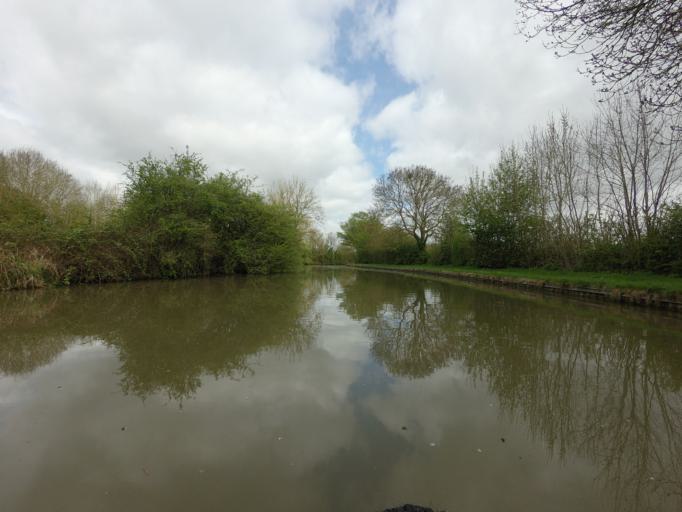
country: GB
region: England
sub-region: Milton Keynes
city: Water Eaton
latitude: 51.9661
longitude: -0.7164
